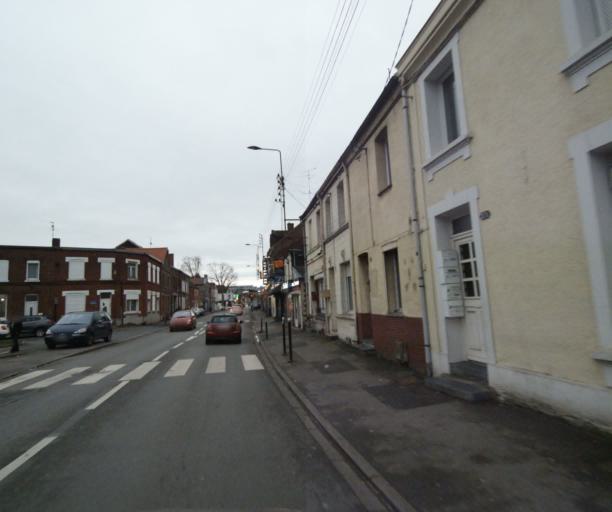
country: FR
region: Nord-Pas-de-Calais
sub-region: Departement du Nord
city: Petite-Foret
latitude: 50.3631
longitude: 3.4920
